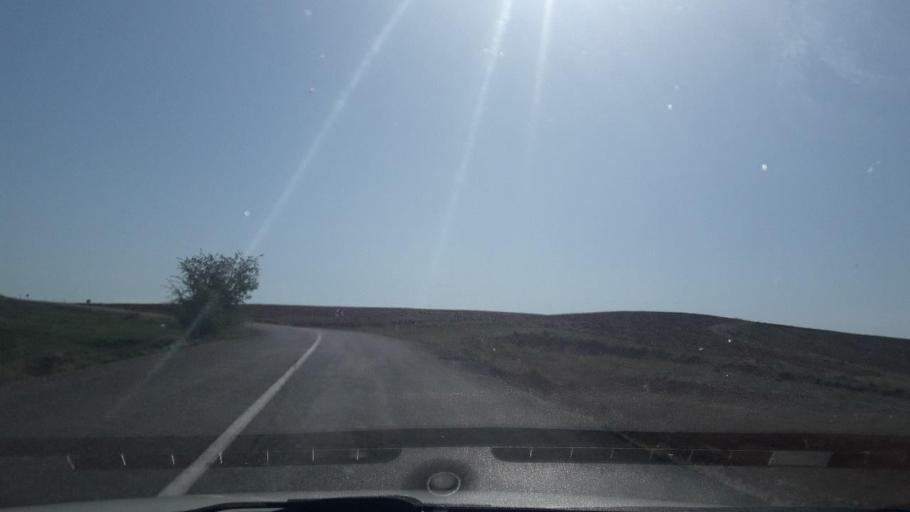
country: TR
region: Sivas
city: Alacahan
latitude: 39.0765
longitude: 37.5510
